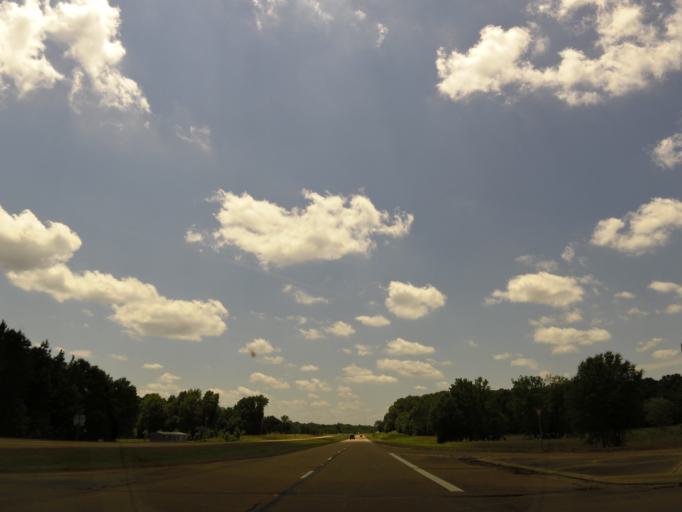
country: US
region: Mississippi
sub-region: Pontotoc County
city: Pontotoc
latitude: 34.2840
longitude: -89.1047
